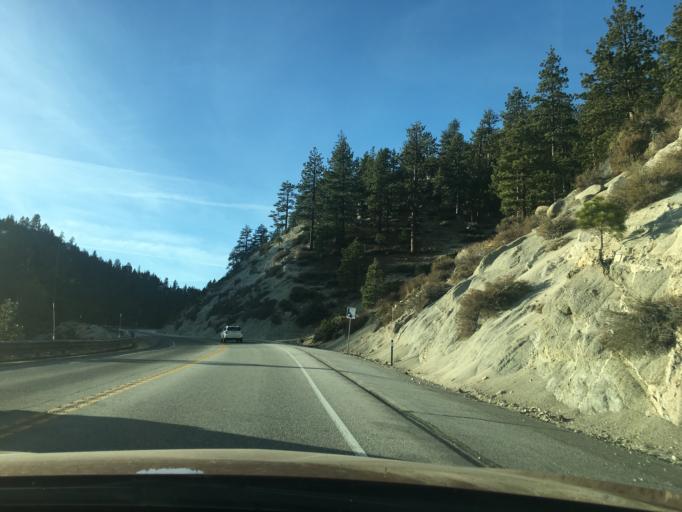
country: US
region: Nevada
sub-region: Douglas County
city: Kingsbury
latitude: 38.9743
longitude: -119.8752
